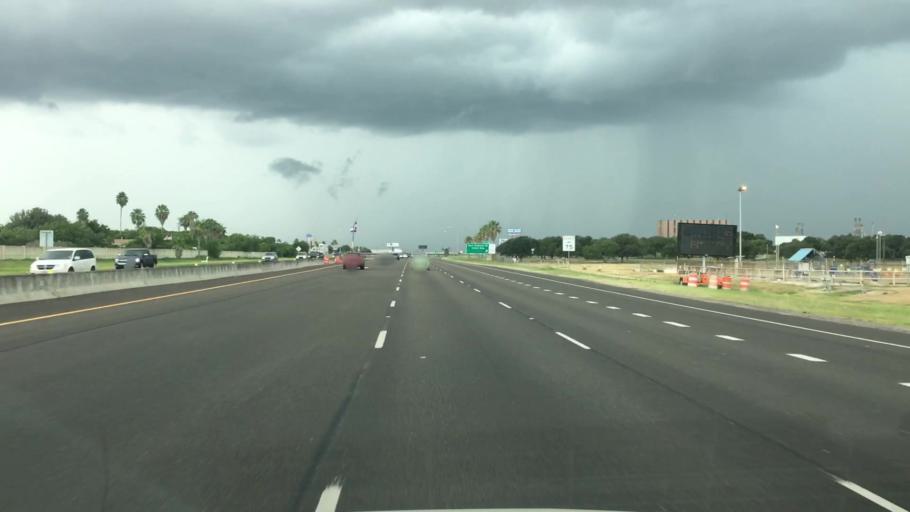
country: US
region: Texas
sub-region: Nueces County
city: Corpus Christi
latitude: 27.8046
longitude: -97.4774
